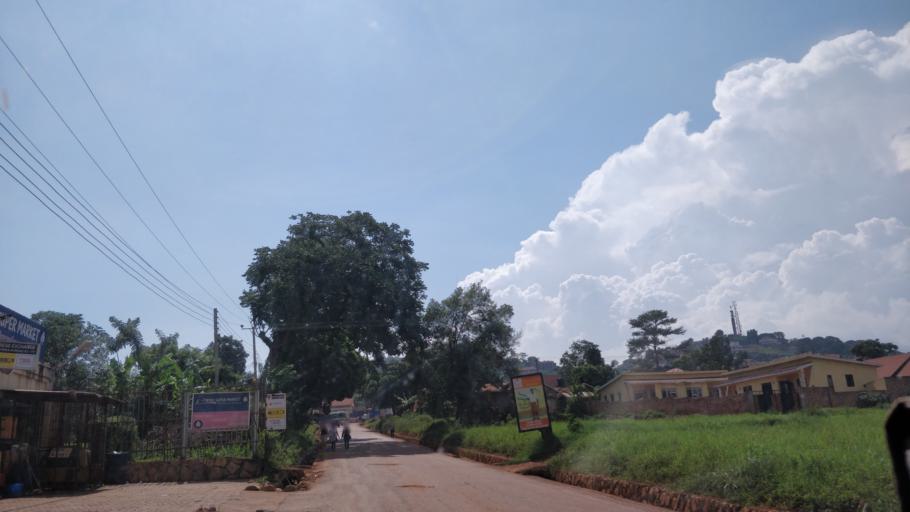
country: UG
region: Central Region
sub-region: Kampala District
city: Kampala
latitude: 0.2683
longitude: 32.6155
